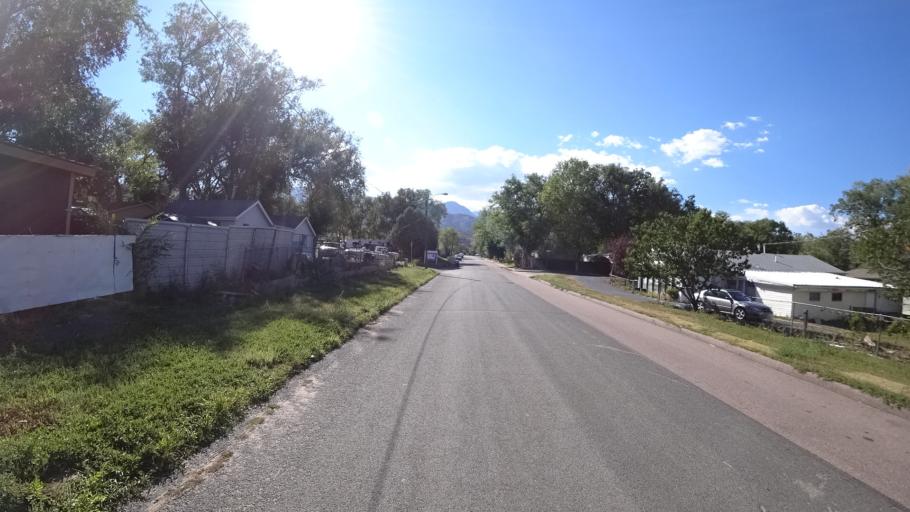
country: US
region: Colorado
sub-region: El Paso County
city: Colorado Springs
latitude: 38.8343
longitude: -104.8652
